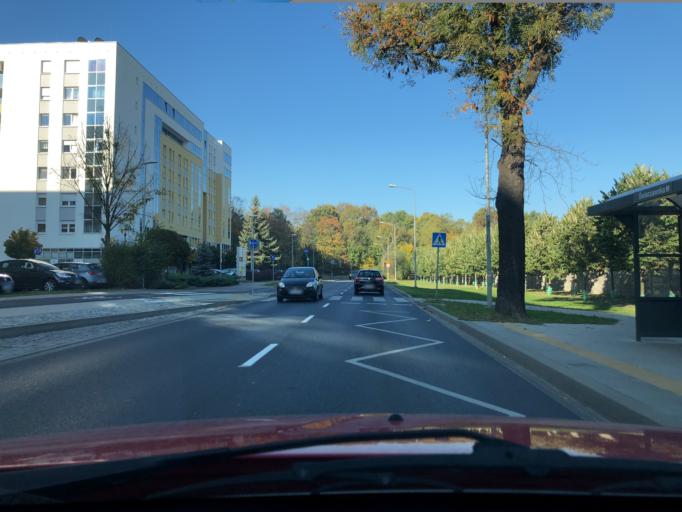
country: PL
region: Greater Poland Voivodeship
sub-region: Powiat poznanski
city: Plewiska
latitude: 52.4055
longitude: 16.8619
